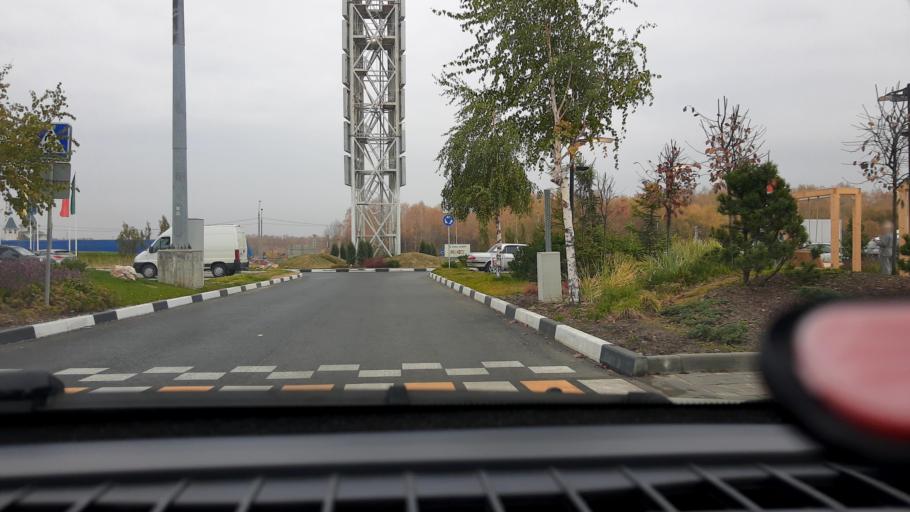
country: RU
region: Nizjnij Novgorod
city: Afonino
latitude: 56.2265
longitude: 44.0718
